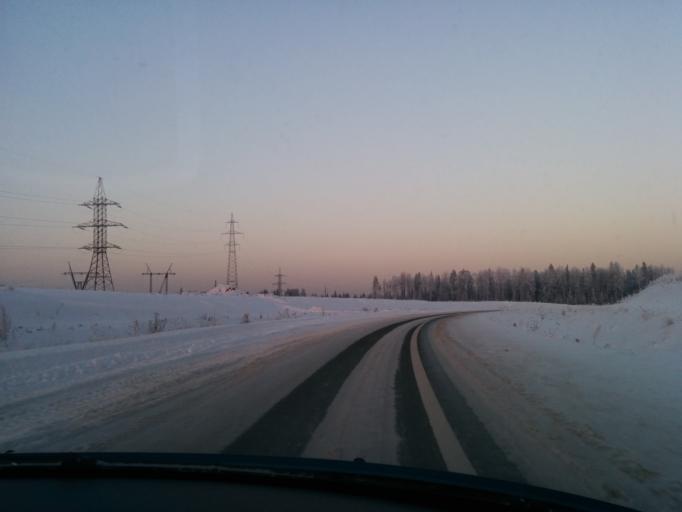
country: RU
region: Perm
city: Novyye Lyady
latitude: 58.0423
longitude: 56.4323
